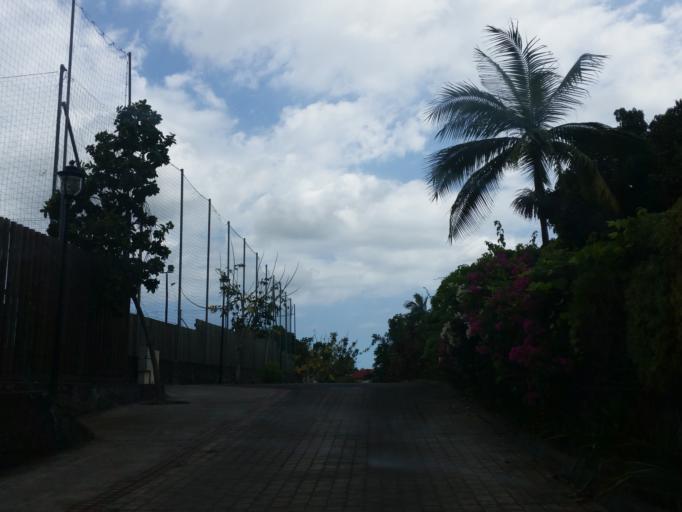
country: RE
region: Reunion
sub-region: Reunion
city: L'Entre-Deux
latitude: -21.2463
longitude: 55.4683
